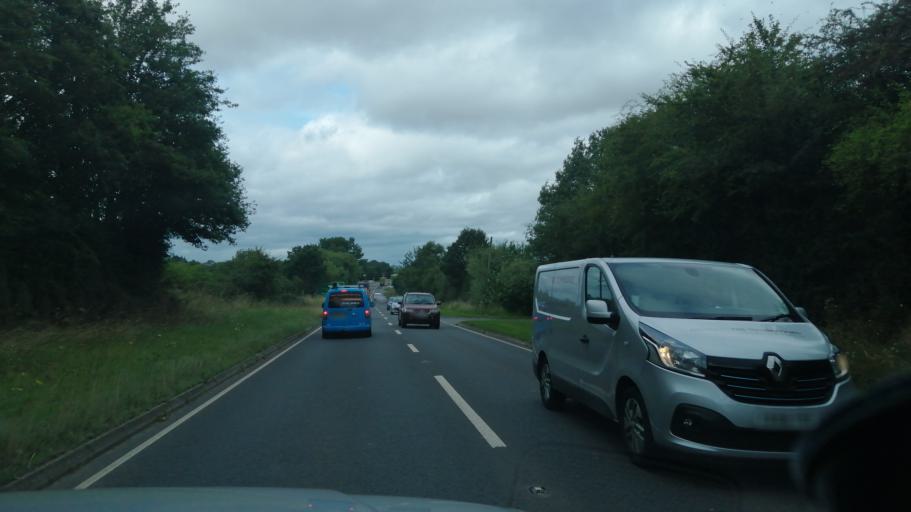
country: GB
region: England
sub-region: Herefordshire
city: Thruxton
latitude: 51.9960
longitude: -2.7915
